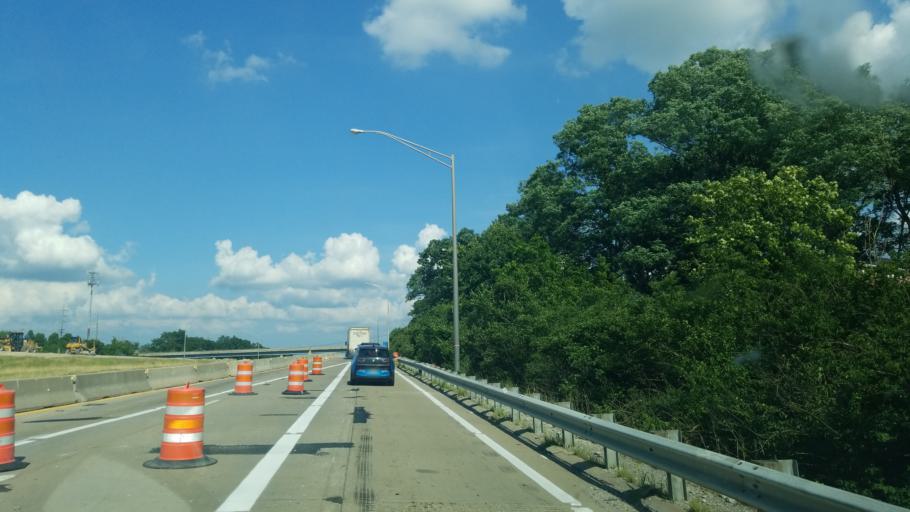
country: US
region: Kentucky
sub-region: Kenton County
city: Crestview Hills
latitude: 39.0325
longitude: -84.5967
